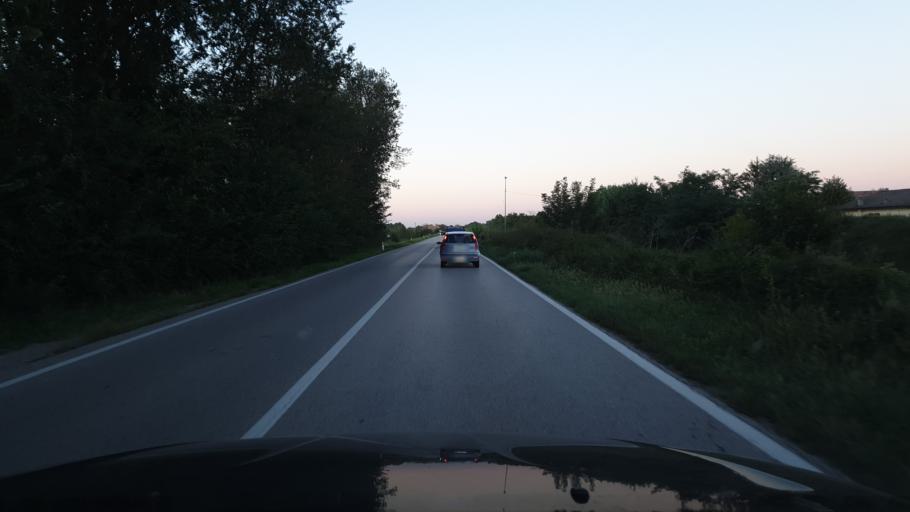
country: IT
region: Emilia-Romagna
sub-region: Provincia di Bologna
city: Ca De Fabbri
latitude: 44.6097
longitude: 11.4464
